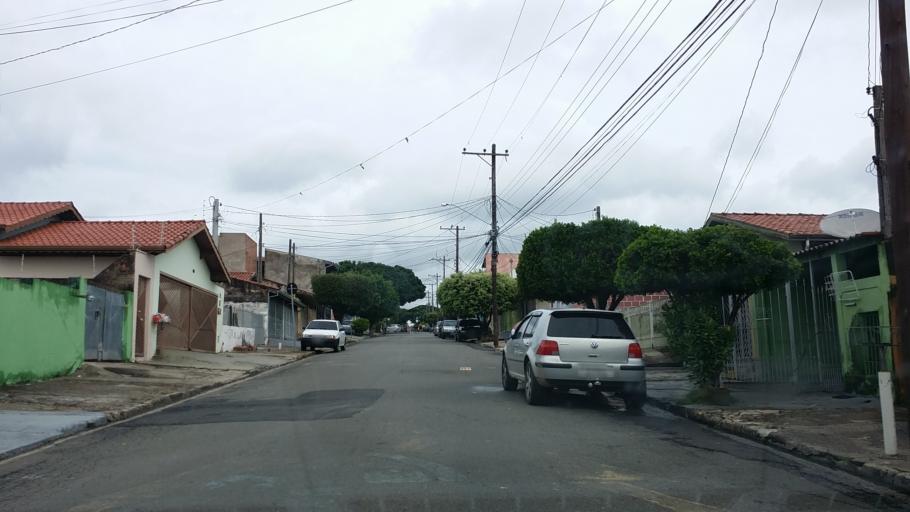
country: BR
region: Sao Paulo
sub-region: Indaiatuba
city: Indaiatuba
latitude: -23.1201
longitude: -47.2289
